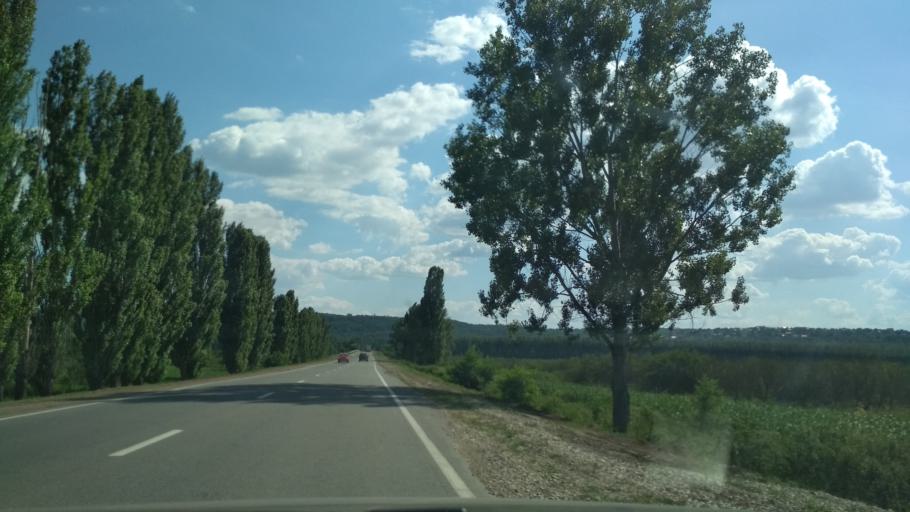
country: MD
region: Chisinau
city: Vadul lui Voda
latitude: 47.0969
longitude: 29.0960
